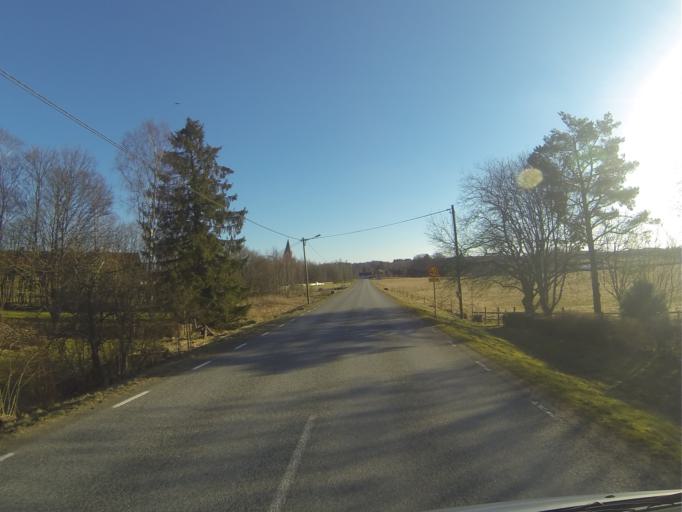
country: SE
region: Skane
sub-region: Horby Kommun
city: Hoerby
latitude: 55.9278
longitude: 13.6683
